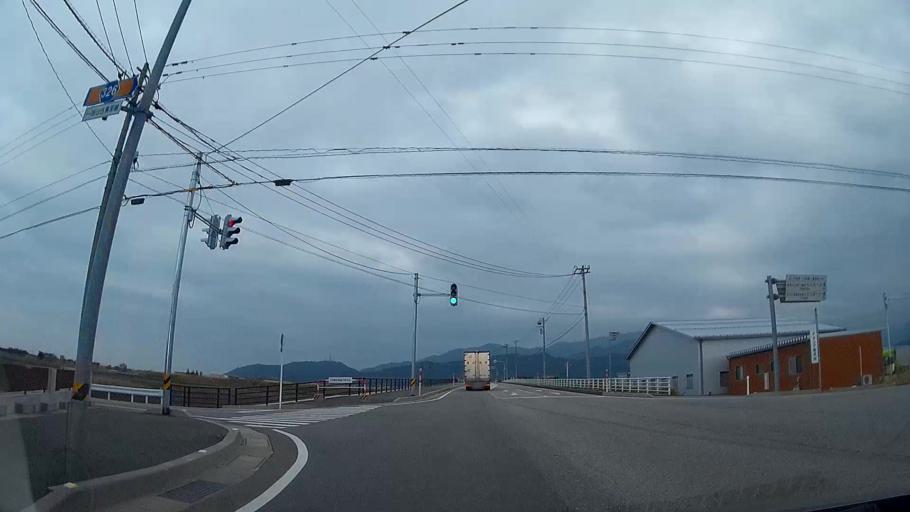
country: JP
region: Toyama
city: Nyuzen
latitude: 36.9457
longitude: 137.5377
